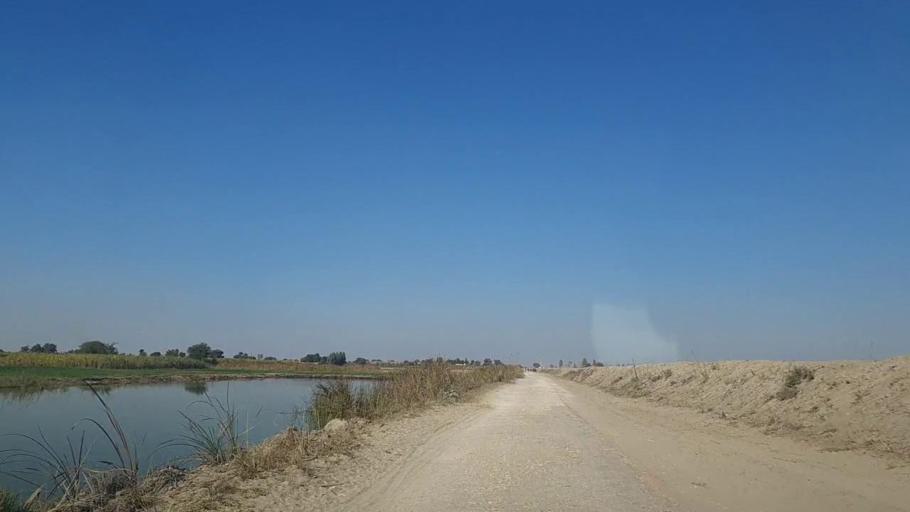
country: PK
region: Sindh
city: Sanghar
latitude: 26.2148
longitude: 68.9292
